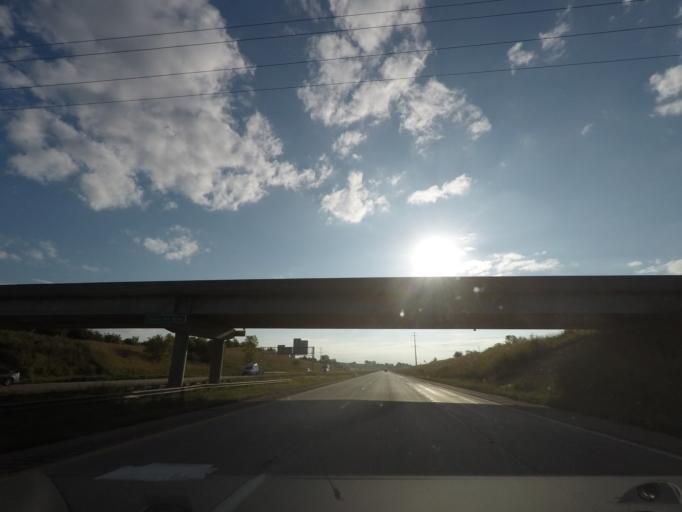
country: US
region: Iowa
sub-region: Warren County
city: Norwalk
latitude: 41.4981
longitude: -93.6165
